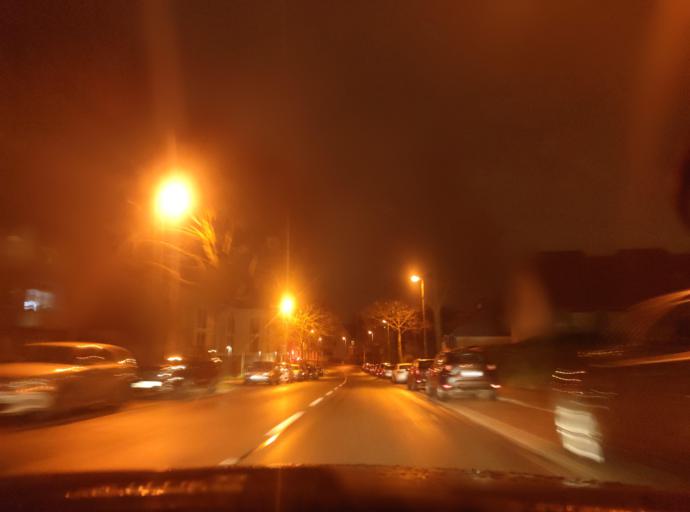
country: DE
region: North Rhine-Westphalia
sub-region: Regierungsbezirk Dusseldorf
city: Essen
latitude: 51.4773
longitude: 7.0625
